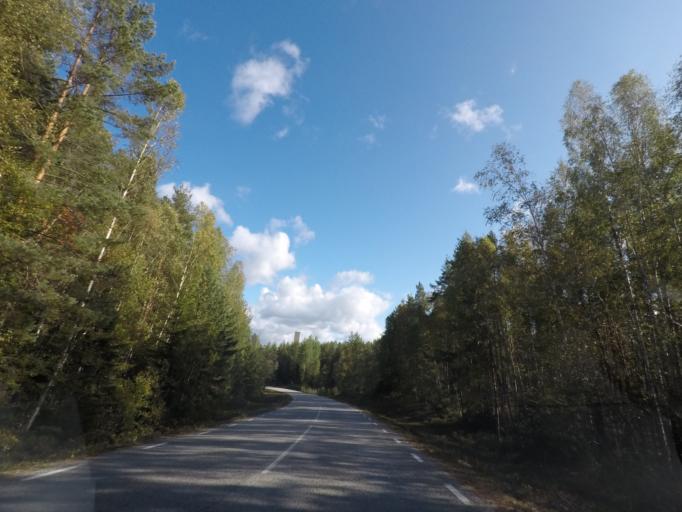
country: SE
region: Vaestmanland
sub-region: Skinnskattebergs Kommun
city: Skinnskatteberg
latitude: 59.8314
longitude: 15.5546
